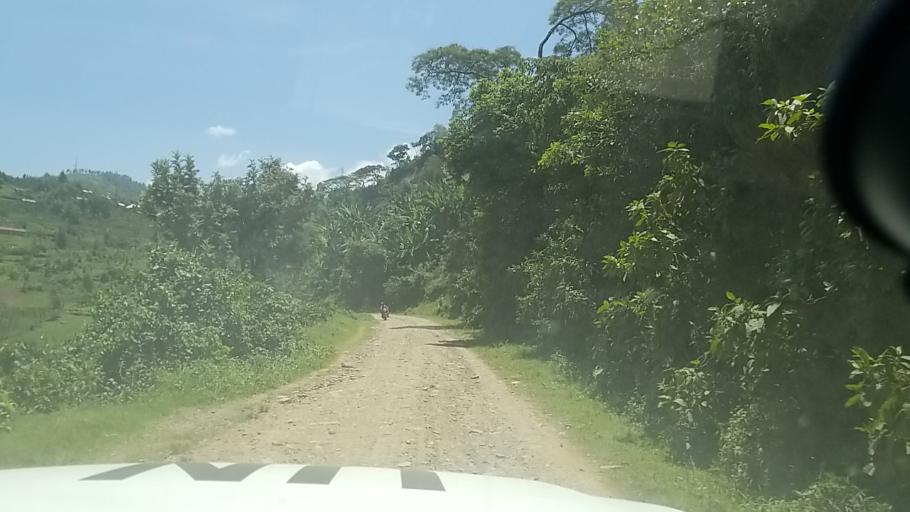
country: CD
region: Nord Kivu
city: Sake
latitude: -1.9143
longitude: 28.9529
